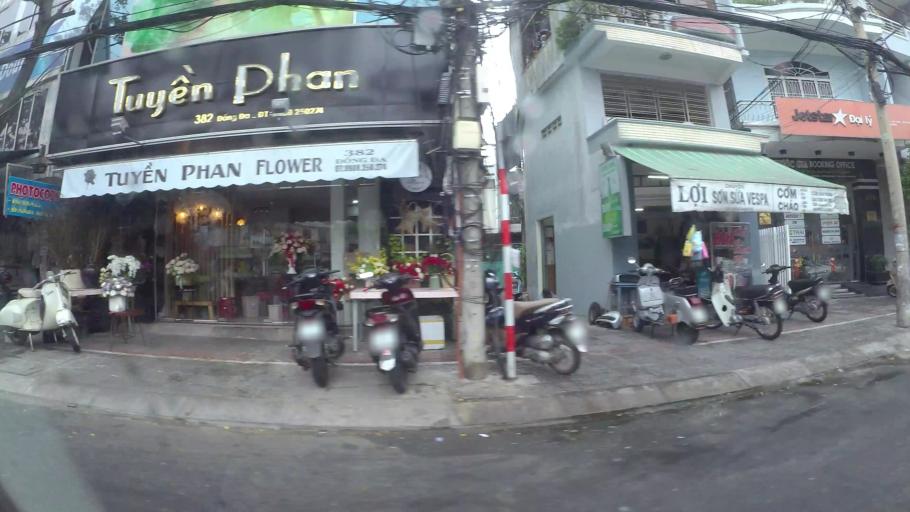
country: VN
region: Da Nang
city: Da Nang
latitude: 16.0741
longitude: 108.2140
